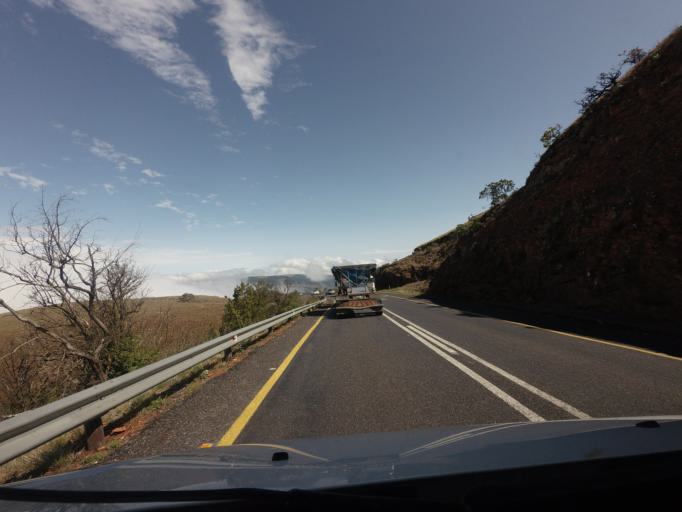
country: ZA
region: Mpumalanga
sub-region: Ehlanzeni District
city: Lydenburg
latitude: -25.1573
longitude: 30.6259
